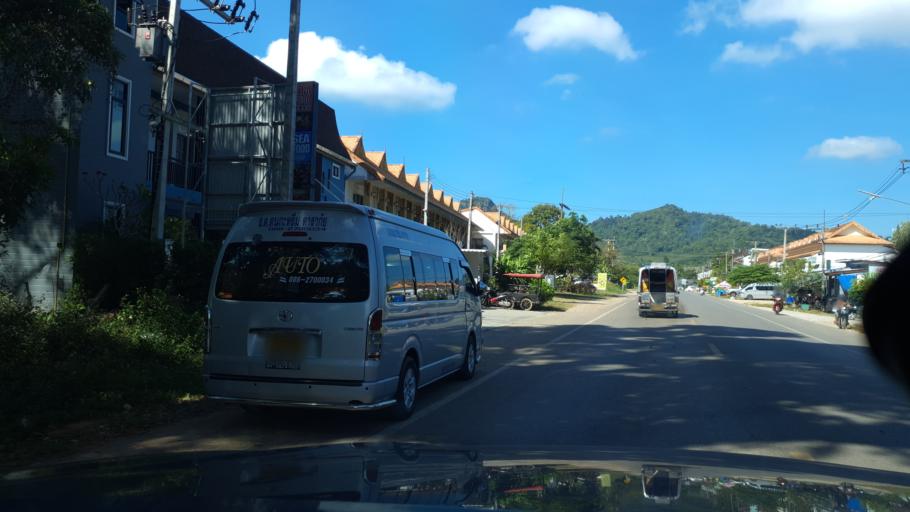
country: TH
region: Phangnga
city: Ban Ao Nang
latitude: 8.0299
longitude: 98.8658
